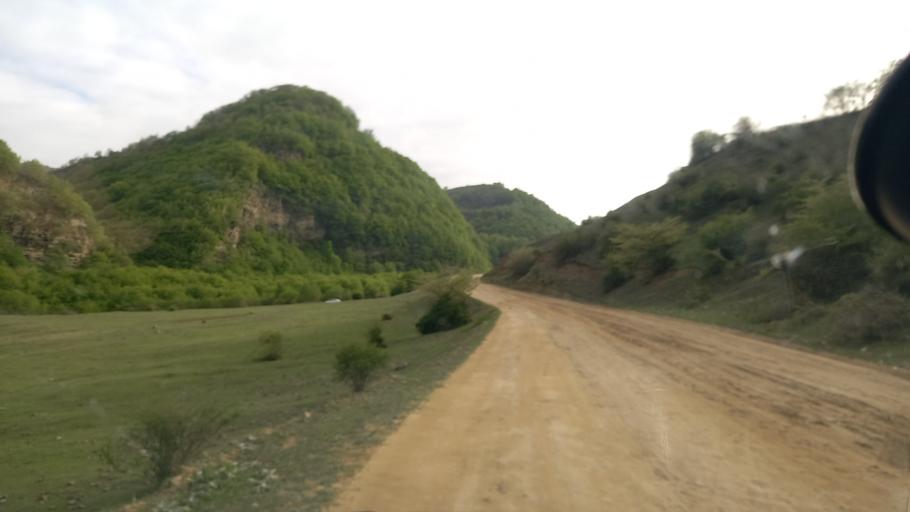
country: RU
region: Dagestan
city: Khuchni
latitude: 41.9632
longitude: 47.8699
